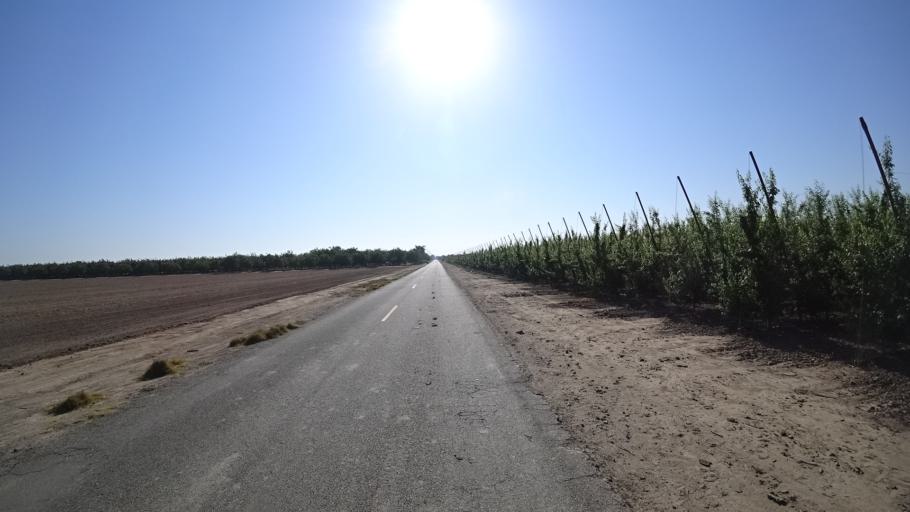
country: US
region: California
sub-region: Kings County
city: Lucerne
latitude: 36.3862
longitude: -119.6702
